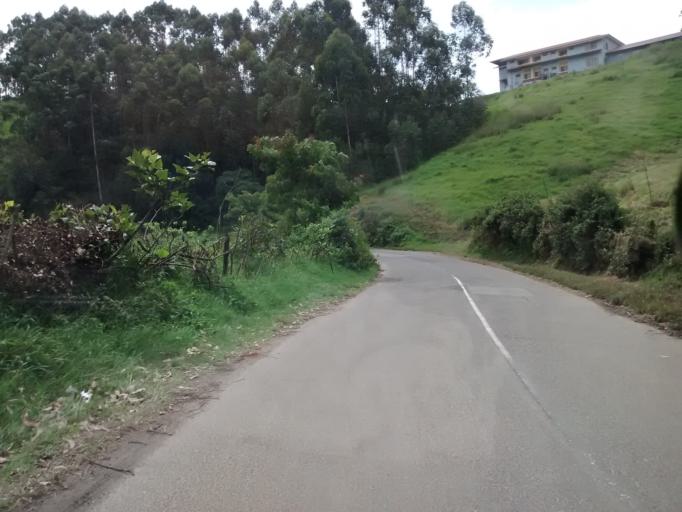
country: IN
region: Kerala
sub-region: Idukki
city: Munnar
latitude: 10.1139
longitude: 77.1351
